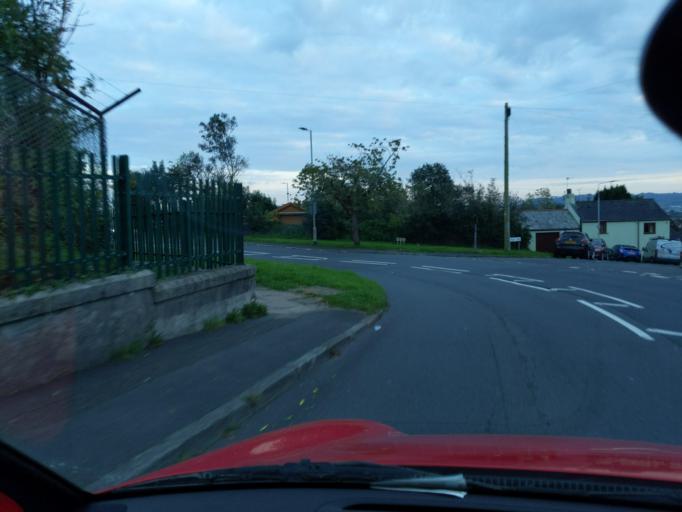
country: GB
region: England
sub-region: Cornwall
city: Torpoint
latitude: 50.4084
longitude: -4.1778
